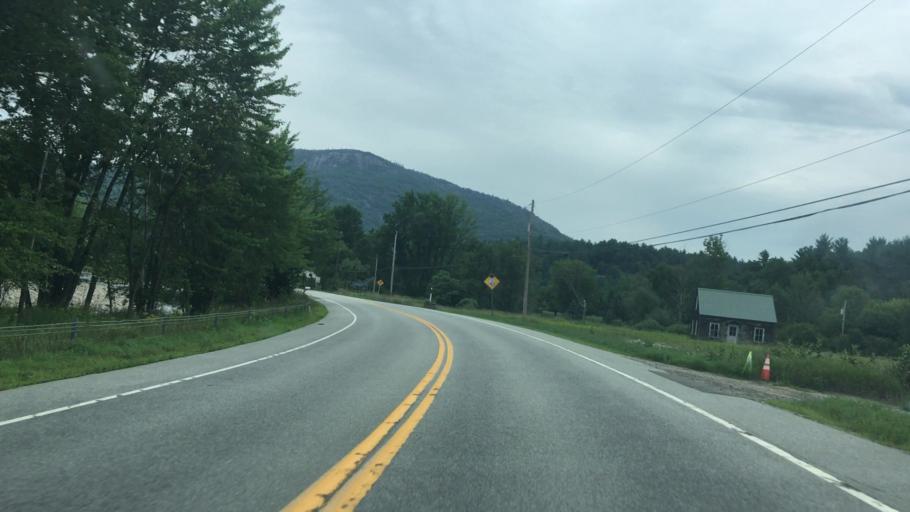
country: US
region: New York
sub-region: Essex County
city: Elizabethtown
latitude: 44.3285
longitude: -73.7733
